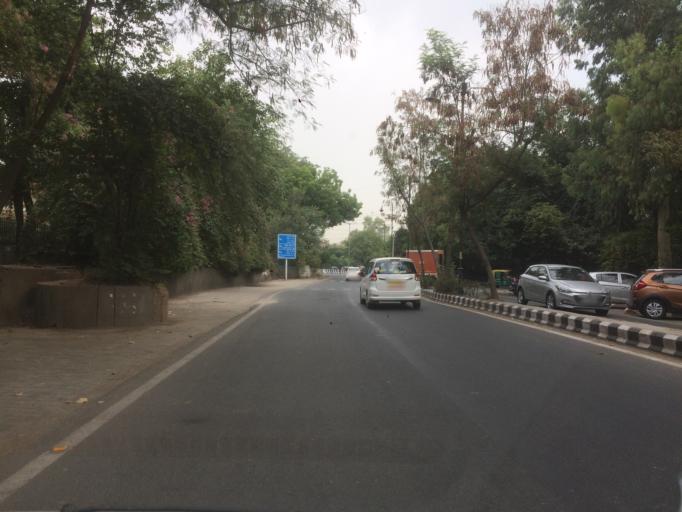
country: IN
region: NCT
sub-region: Central Delhi
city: Karol Bagh
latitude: 28.5722
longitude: 77.1748
